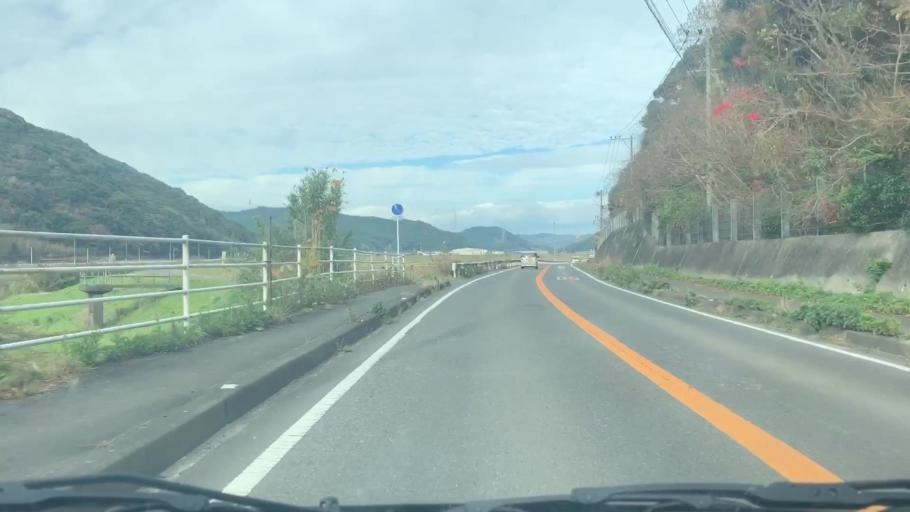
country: JP
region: Saga Prefecture
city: Karatsu
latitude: 33.3645
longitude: 130.0072
